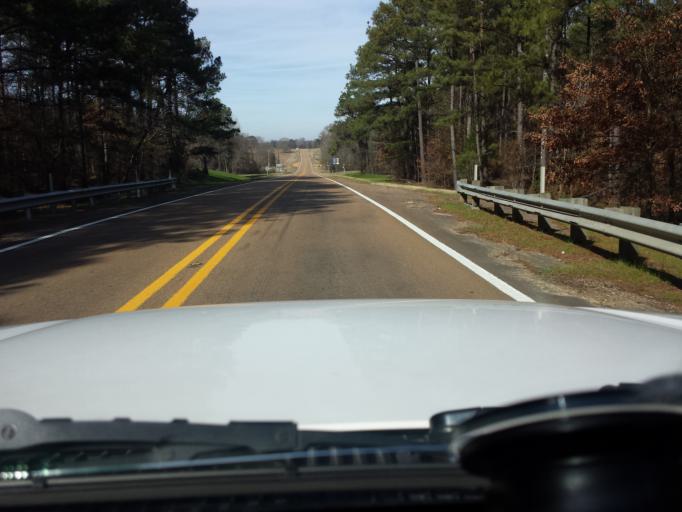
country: US
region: Mississippi
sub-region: Madison County
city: Canton
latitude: 32.6825
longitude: -90.0575
